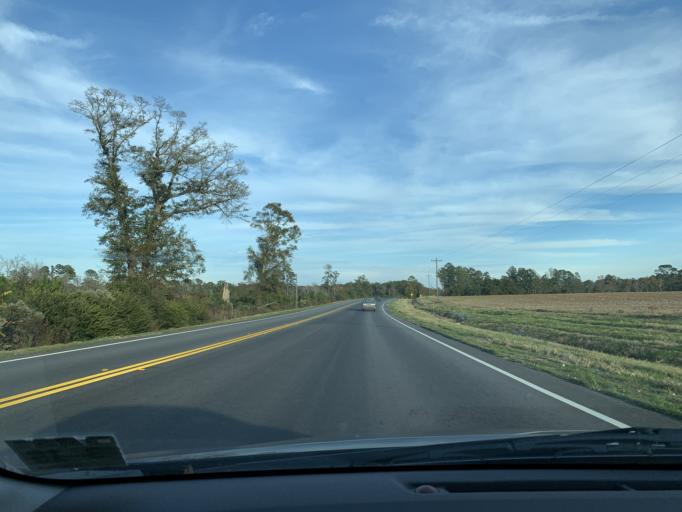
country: US
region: Georgia
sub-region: Irwin County
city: Ocilla
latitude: 31.5957
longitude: -83.1797
